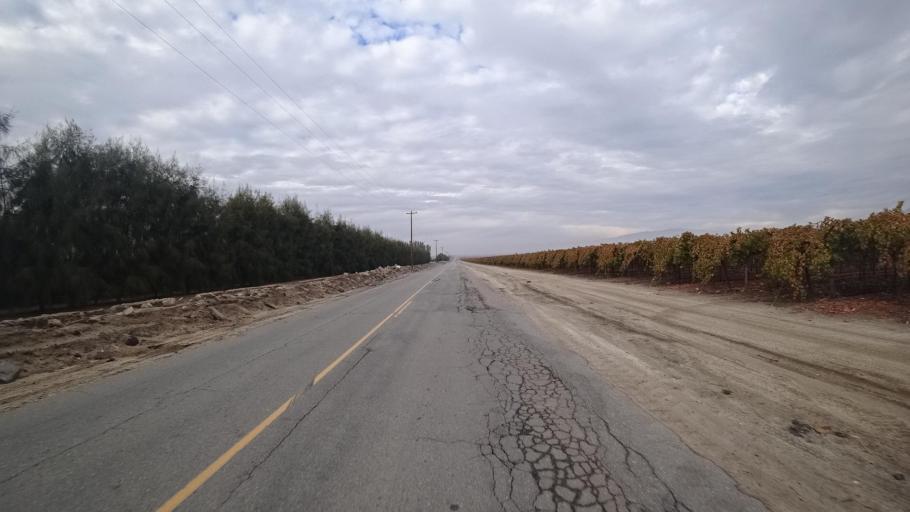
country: US
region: California
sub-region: Kern County
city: Arvin
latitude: 35.1521
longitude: -118.8235
